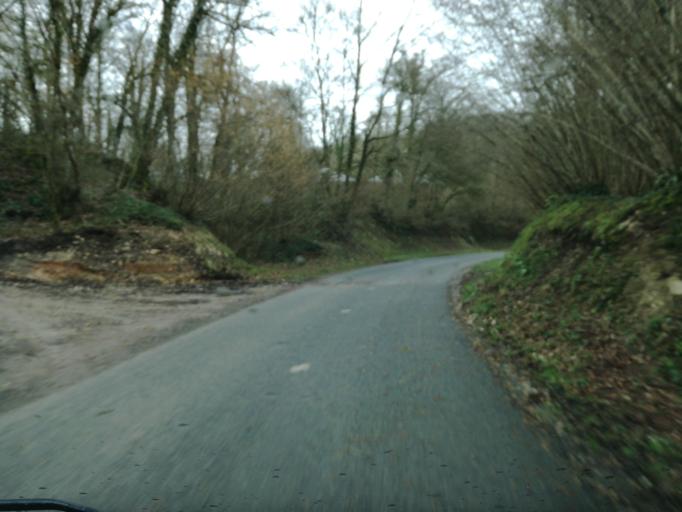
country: FR
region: Haute-Normandie
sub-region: Departement de la Seine-Maritime
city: Saint-Wandrille-Rancon
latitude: 49.5569
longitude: 0.7509
